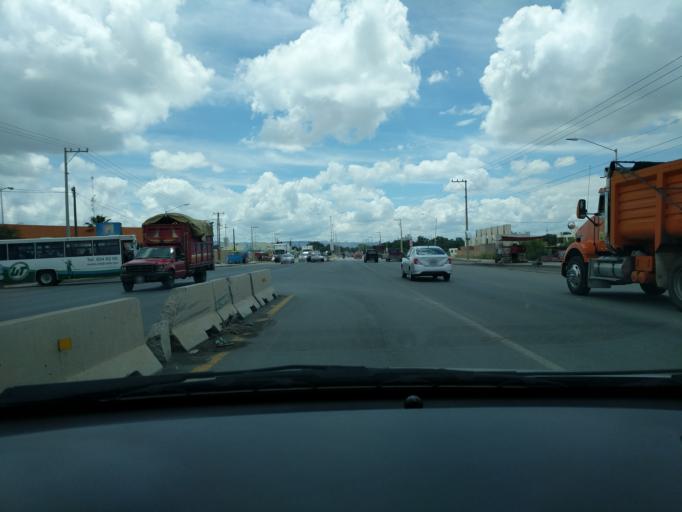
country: MX
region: San Luis Potosi
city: Soledad Diez Gutierrez
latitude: 22.2138
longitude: -100.9384
